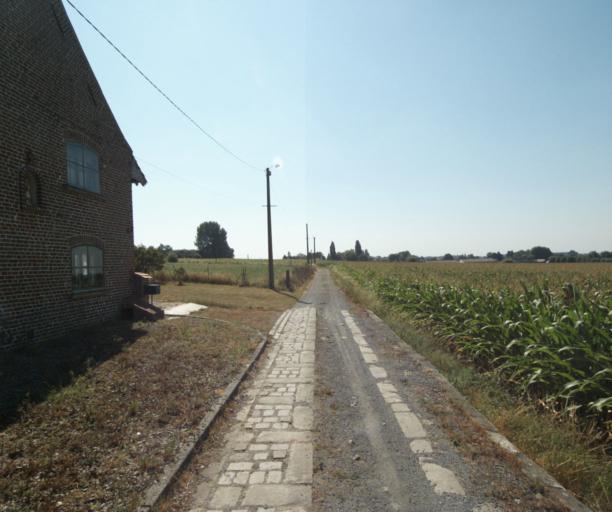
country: FR
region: Nord-Pas-de-Calais
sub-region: Departement du Nord
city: Linselles
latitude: 50.7528
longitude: 3.0756
